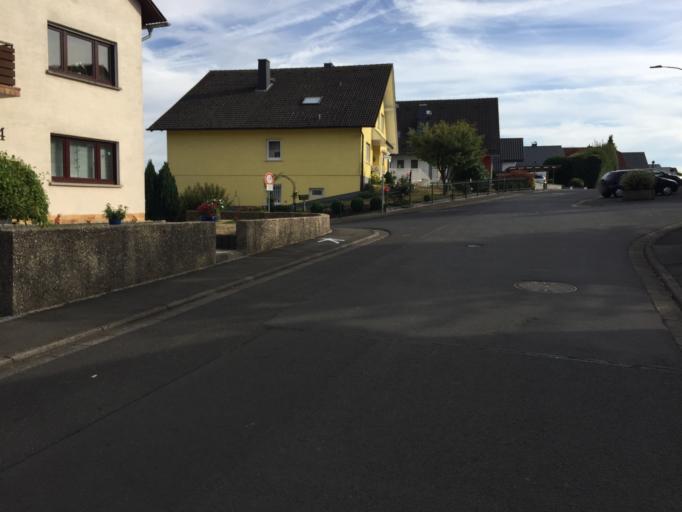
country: DE
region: Hesse
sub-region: Regierungsbezirk Giessen
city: Langgons
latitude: 50.5092
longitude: 8.7338
